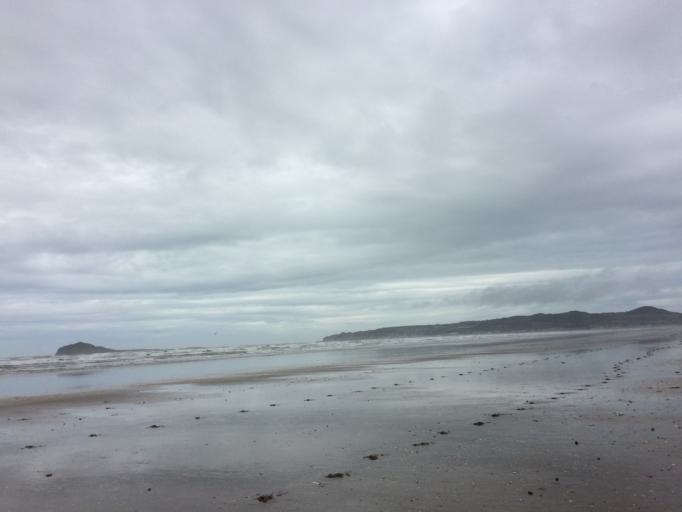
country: IE
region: Leinster
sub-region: Fingal County
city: Baldoyle
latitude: 53.4145
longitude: -6.1183
